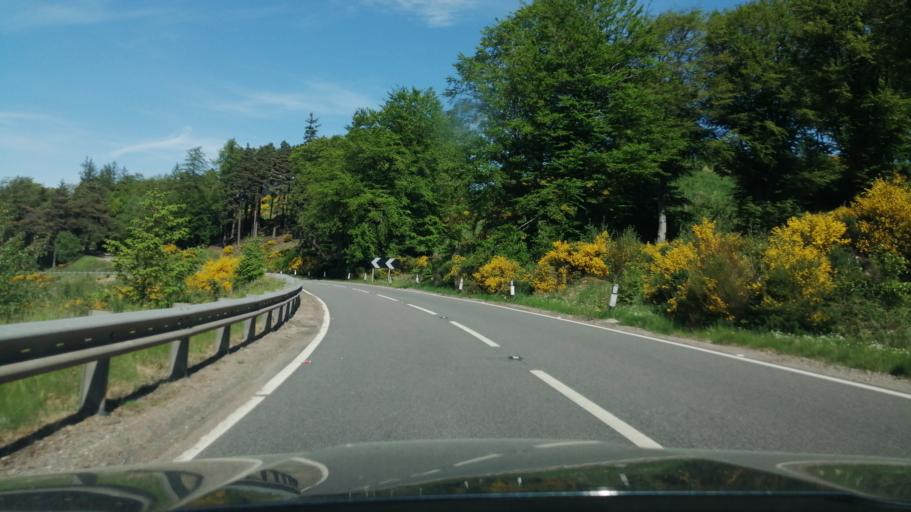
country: GB
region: Scotland
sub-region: Moray
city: Rothes
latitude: 57.4883
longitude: -3.1680
